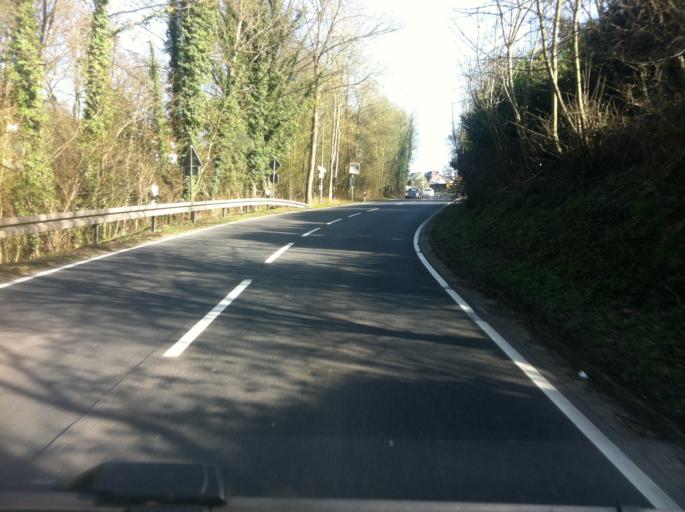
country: DE
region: North Rhine-Westphalia
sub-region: Regierungsbezirk Koln
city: Nideggen
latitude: 50.6932
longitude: 6.4806
